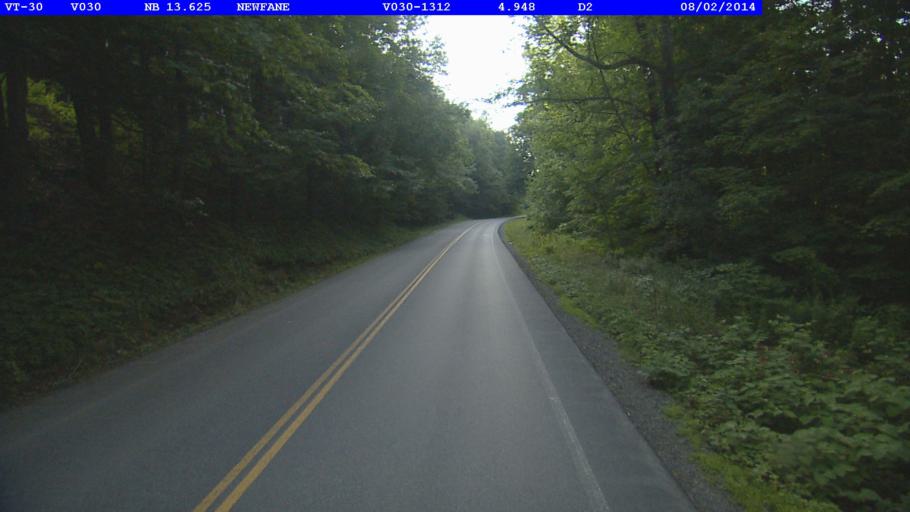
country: US
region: Vermont
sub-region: Windham County
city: Newfane
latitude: 43.0112
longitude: -72.6483
